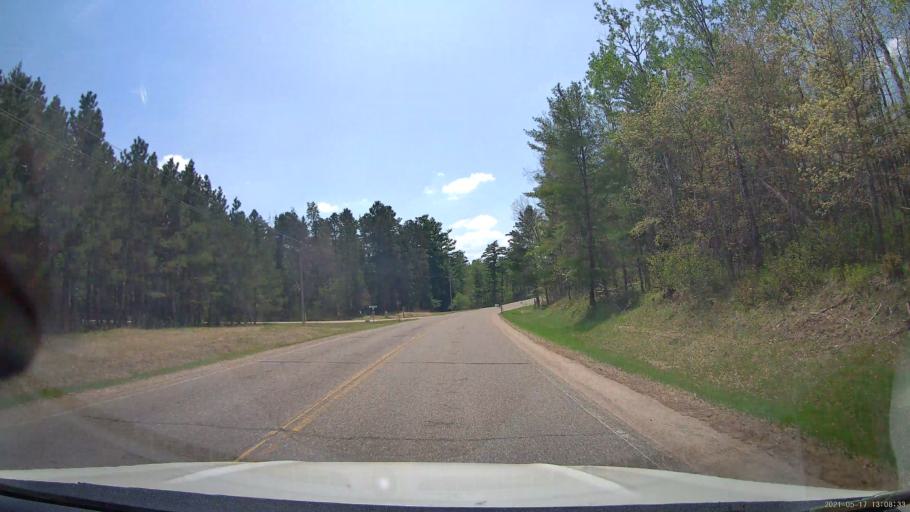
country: US
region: Minnesota
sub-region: Hubbard County
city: Park Rapids
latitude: 47.0362
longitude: -94.9180
